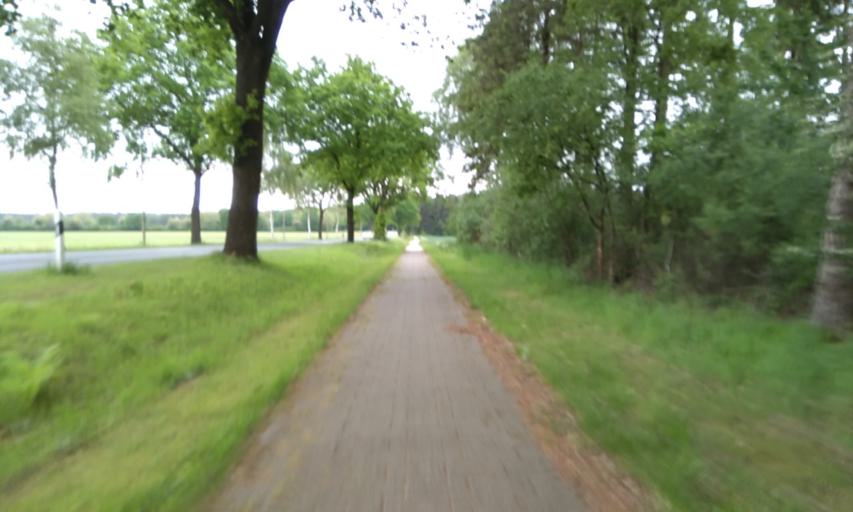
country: DE
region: Lower Saxony
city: Harsefeld
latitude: 53.4891
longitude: 9.4927
